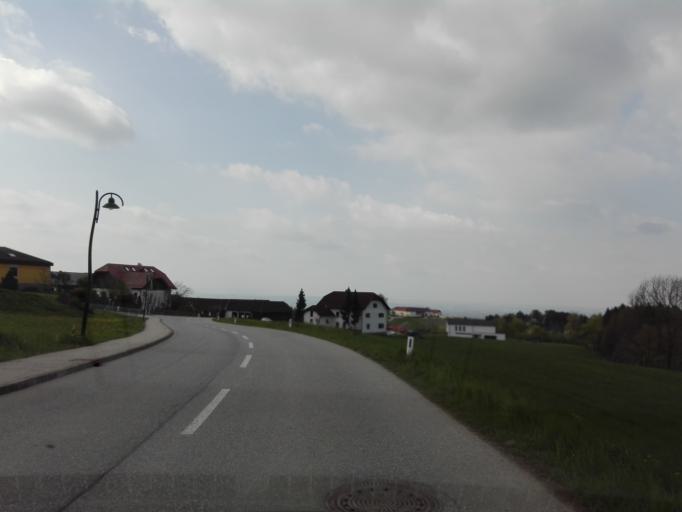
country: AT
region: Upper Austria
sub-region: Politischer Bezirk Perg
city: Perg
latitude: 48.2837
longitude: 14.6786
